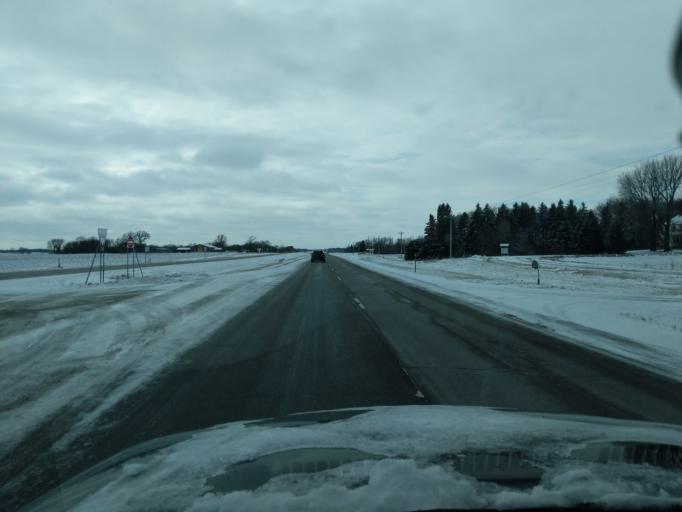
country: US
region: Minnesota
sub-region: McLeod County
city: Glencoe
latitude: 44.7682
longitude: -94.0503
